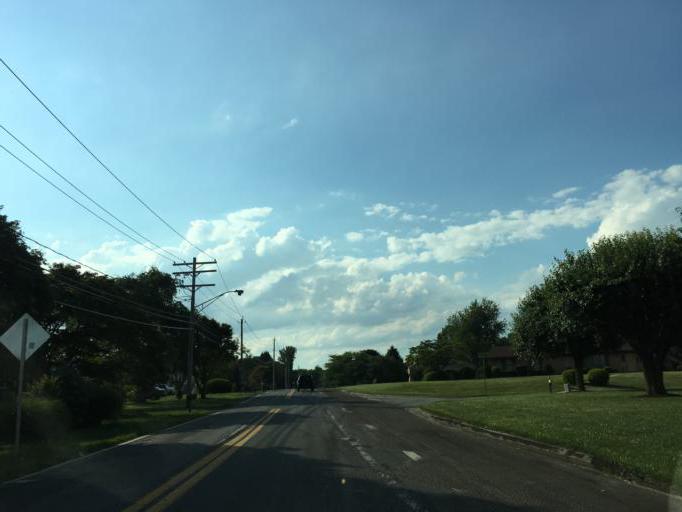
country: US
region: Maryland
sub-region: Baltimore County
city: Kingsville
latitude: 39.4370
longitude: -76.4346
